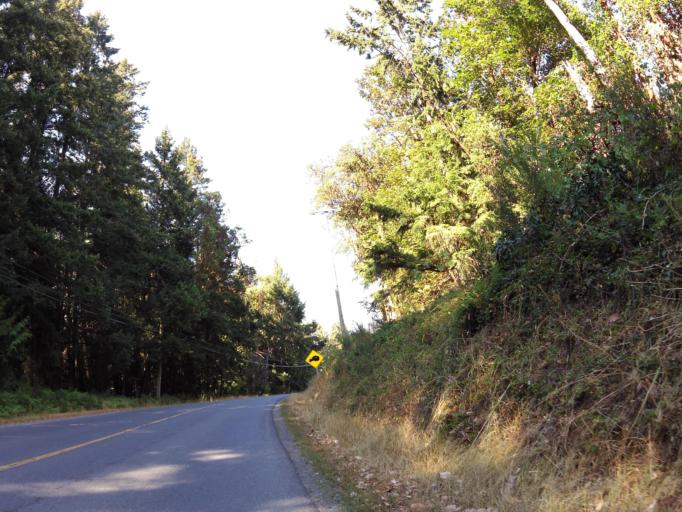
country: CA
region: British Columbia
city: North Saanich
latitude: 48.6729
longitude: -123.5524
